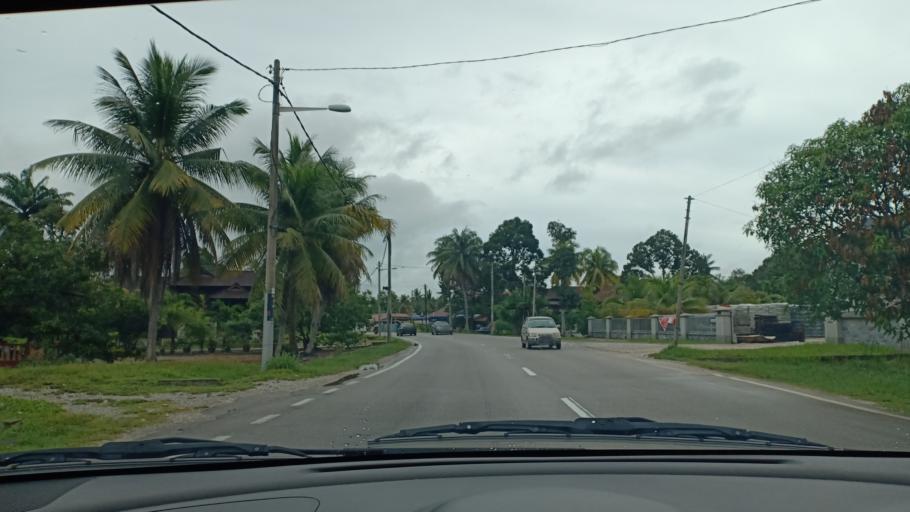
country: MY
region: Penang
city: Kepala Batas
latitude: 5.4963
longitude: 100.4453
